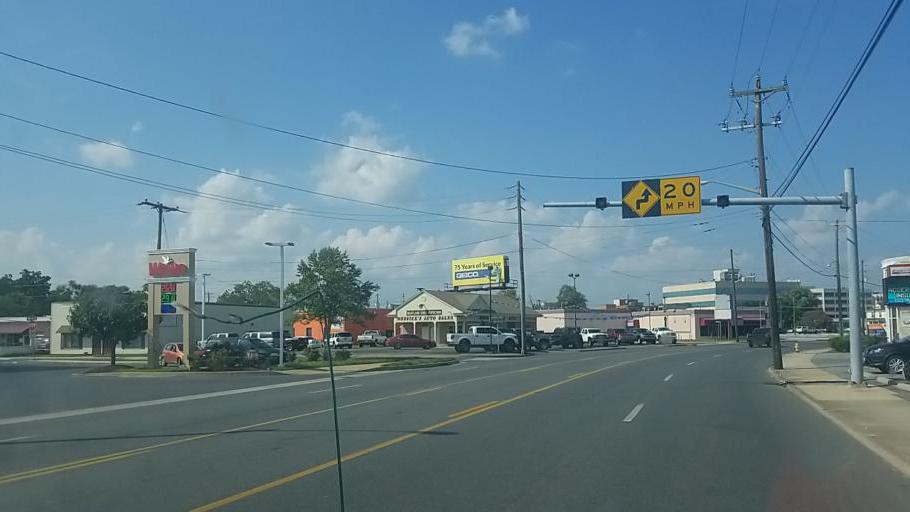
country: US
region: Maryland
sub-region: Wicomico County
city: Salisbury
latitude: 38.3579
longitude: -75.5997
